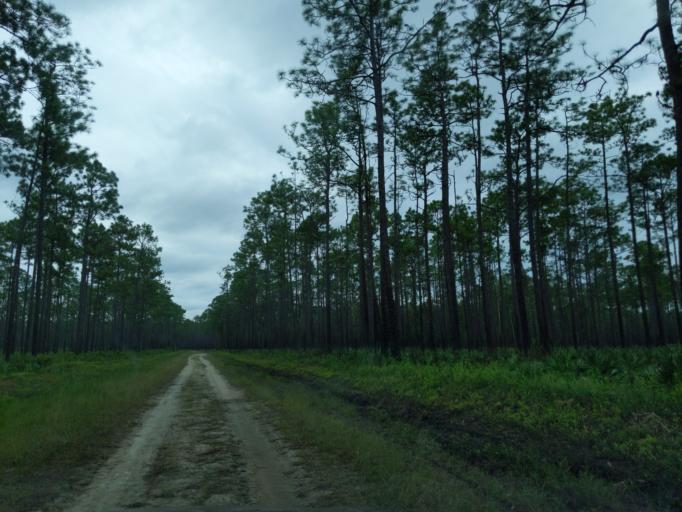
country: US
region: Florida
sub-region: Gadsden County
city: Midway
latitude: 30.3723
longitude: -84.4866
